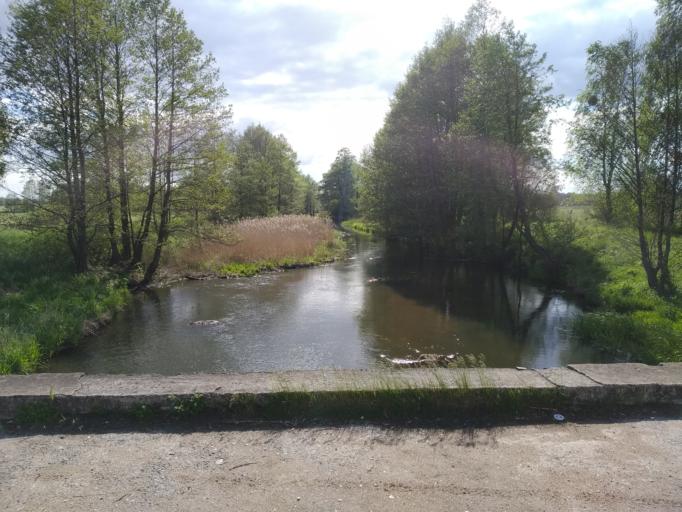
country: BY
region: Grodnenskaya
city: Mir
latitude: 53.6154
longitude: 26.5744
